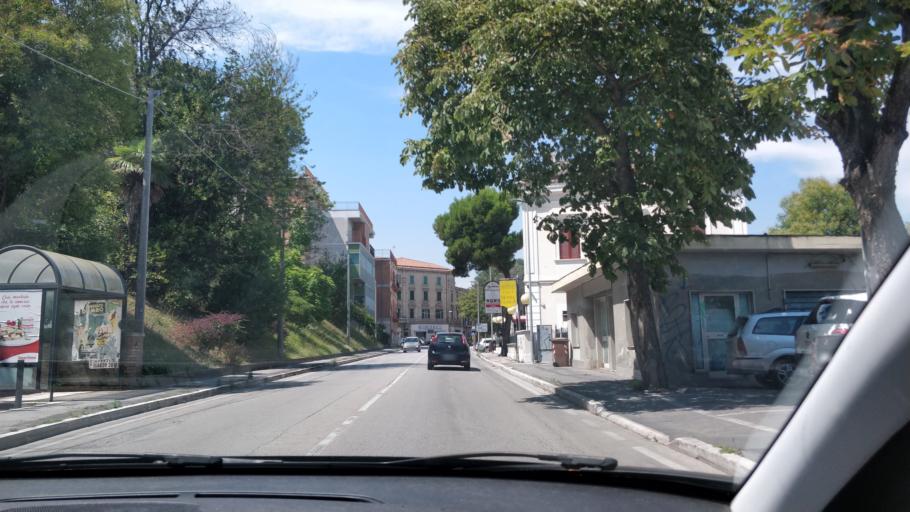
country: IT
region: Abruzzo
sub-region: Provincia di Chieti
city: Francavilla al Mare
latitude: 42.4200
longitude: 14.2910
